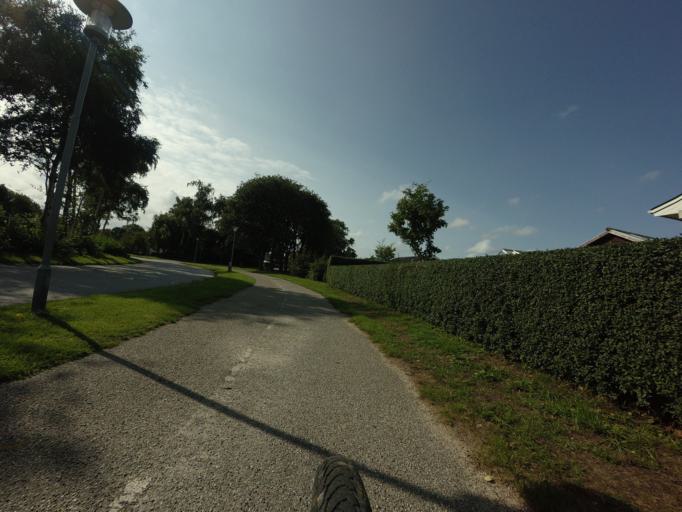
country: DK
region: North Denmark
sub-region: Hjorring Kommune
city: Hjorring
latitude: 57.5153
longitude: 10.0289
